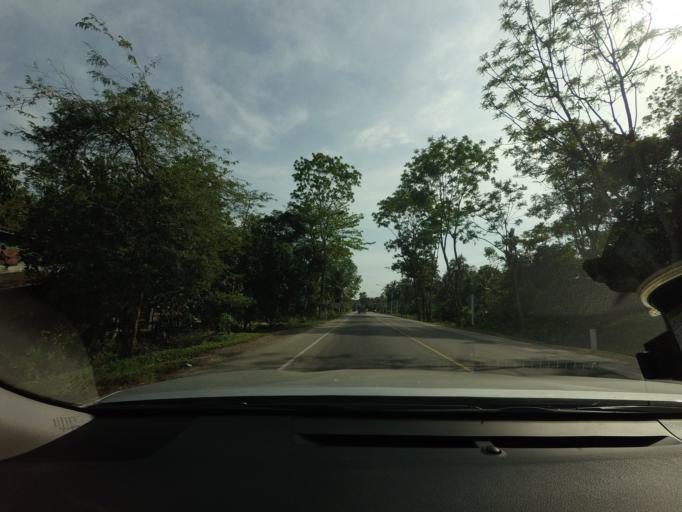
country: TH
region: Narathiwat
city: Ra-ngae
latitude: 6.3236
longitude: 101.7884
